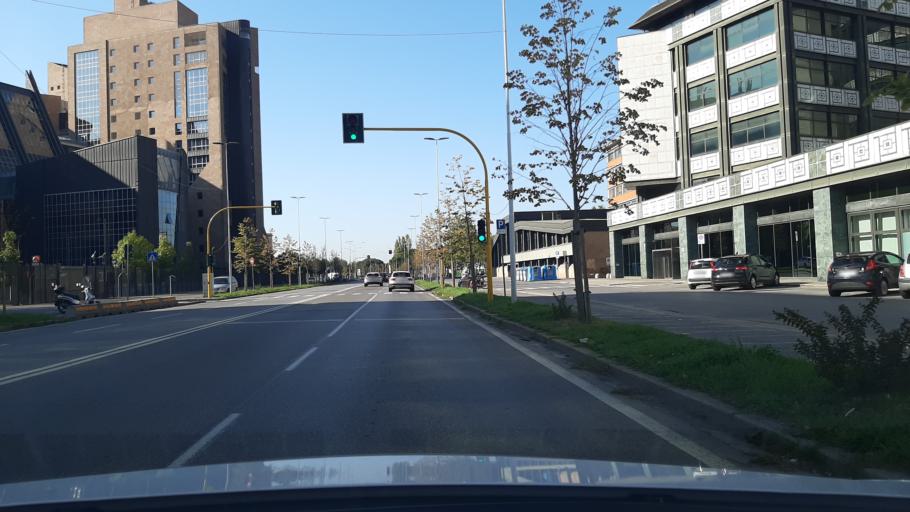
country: IT
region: Tuscany
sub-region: Province of Florence
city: Florence
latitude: 43.7958
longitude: 11.2275
